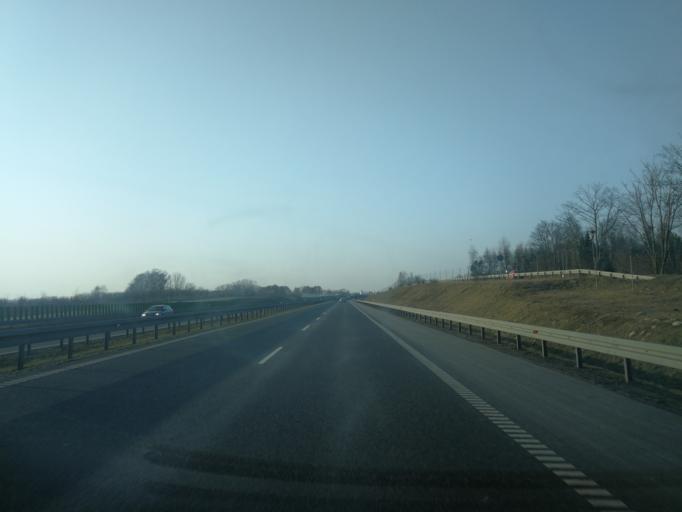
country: PL
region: Warmian-Masurian Voivodeship
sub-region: Powiat elblaski
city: Gronowo Gorne
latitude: 54.1212
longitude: 19.4693
